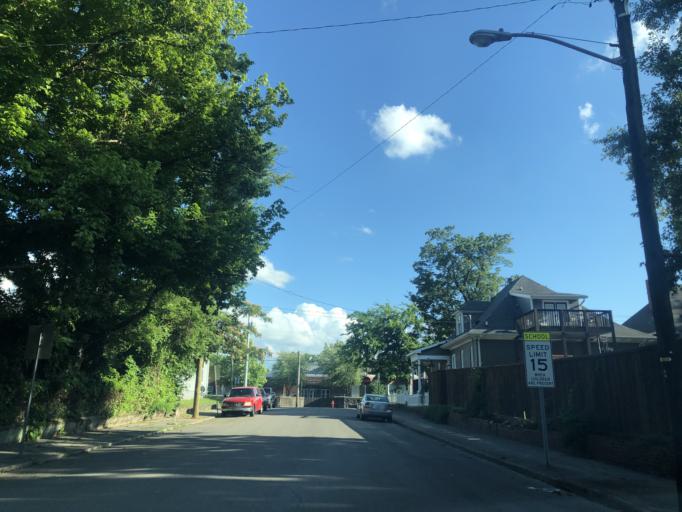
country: US
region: Tennessee
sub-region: Davidson County
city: Nashville
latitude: 36.1876
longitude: -86.7662
